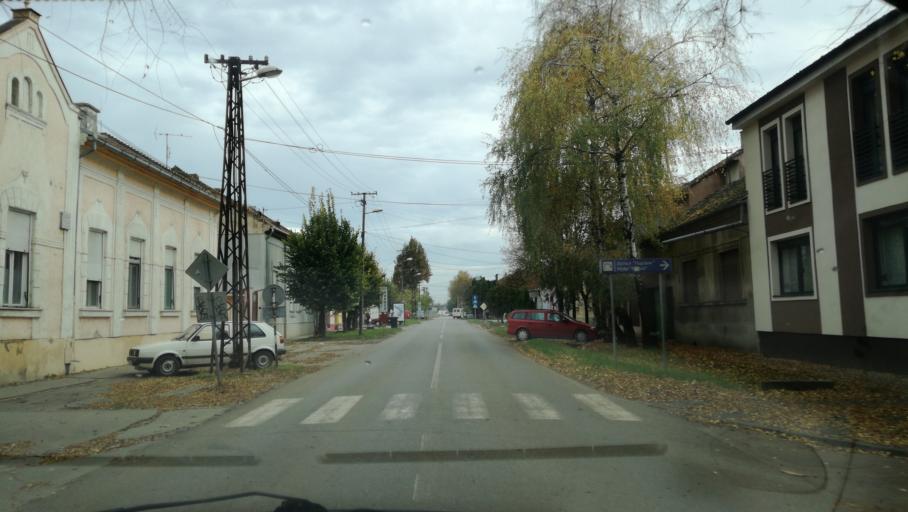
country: RS
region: Autonomna Pokrajina Vojvodina
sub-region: Severnobanatski Okrug
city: Kikinda
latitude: 45.8326
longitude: 20.4720
